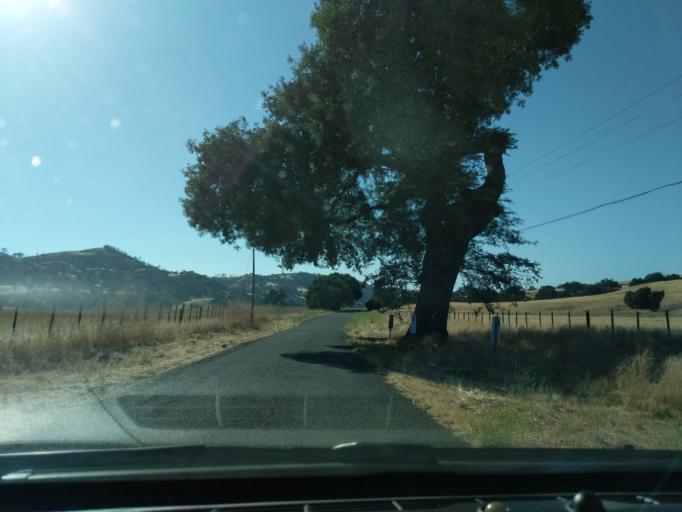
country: US
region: California
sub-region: San Luis Obispo County
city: San Miguel
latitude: 36.1154
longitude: -120.7261
